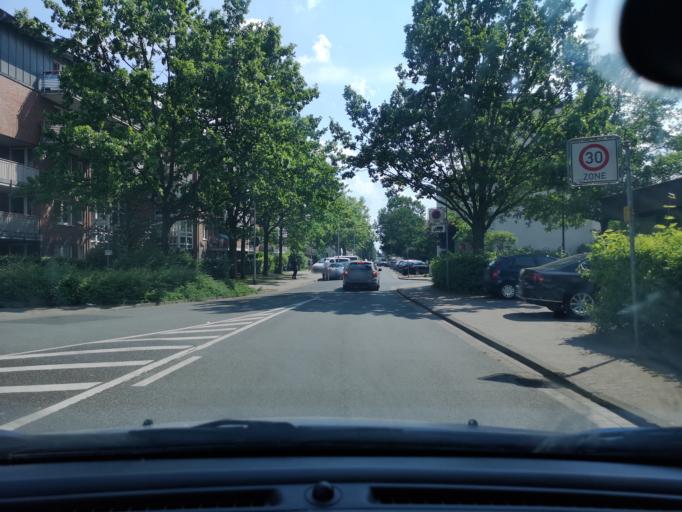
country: DE
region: Lower Saxony
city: Langenhagen
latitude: 52.4376
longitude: 9.7386
